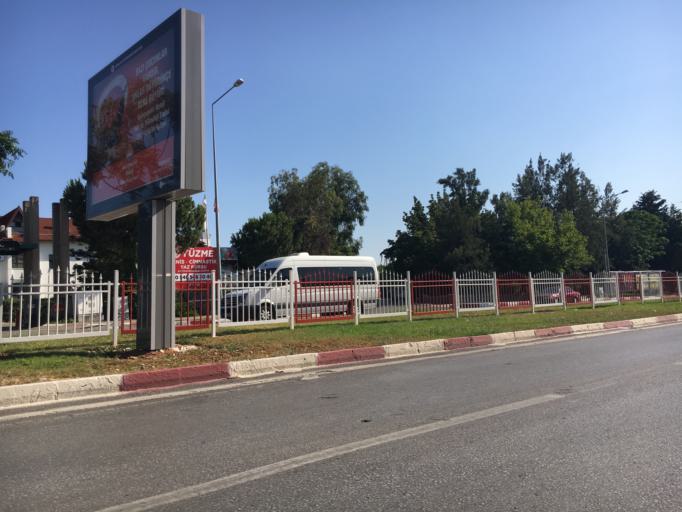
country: TR
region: Antalya
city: Antalya
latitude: 36.8869
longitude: 30.6724
